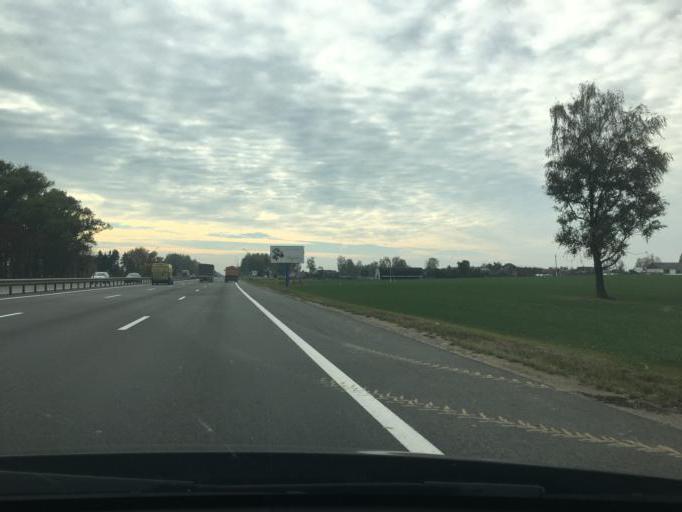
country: BY
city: Fanipol
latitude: 53.7648
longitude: 27.3418
